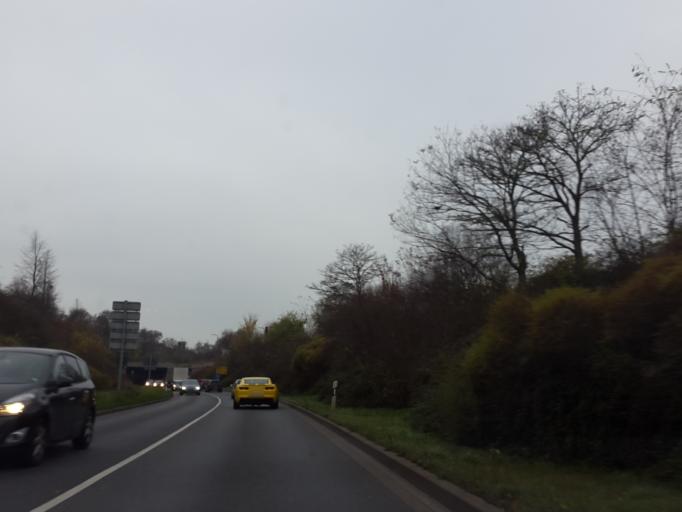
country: DE
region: Bavaria
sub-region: Regierungsbezirk Unterfranken
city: Aschaffenburg
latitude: 49.9668
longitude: 9.1483
